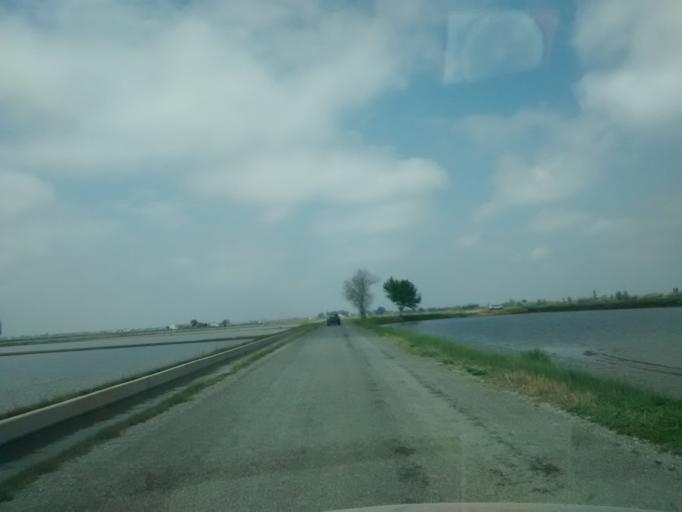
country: ES
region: Catalonia
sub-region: Provincia de Tarragona
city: Deltebre
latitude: 40.6894
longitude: 0.7809
